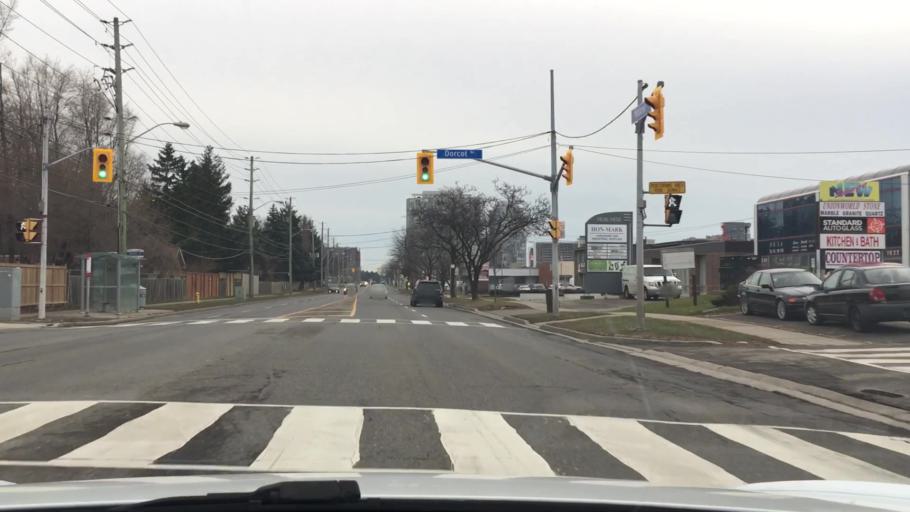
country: CA
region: Ontario
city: Scarborough
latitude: 43.7581
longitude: -79.2675
